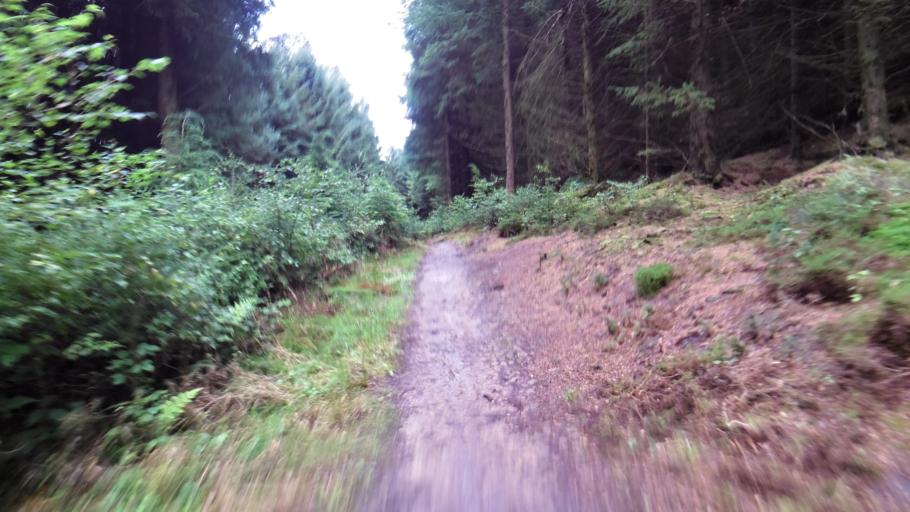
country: GB
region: England
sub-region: North Yorkshire
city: Thornton Dale
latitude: 54.2820
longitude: -0.6857
